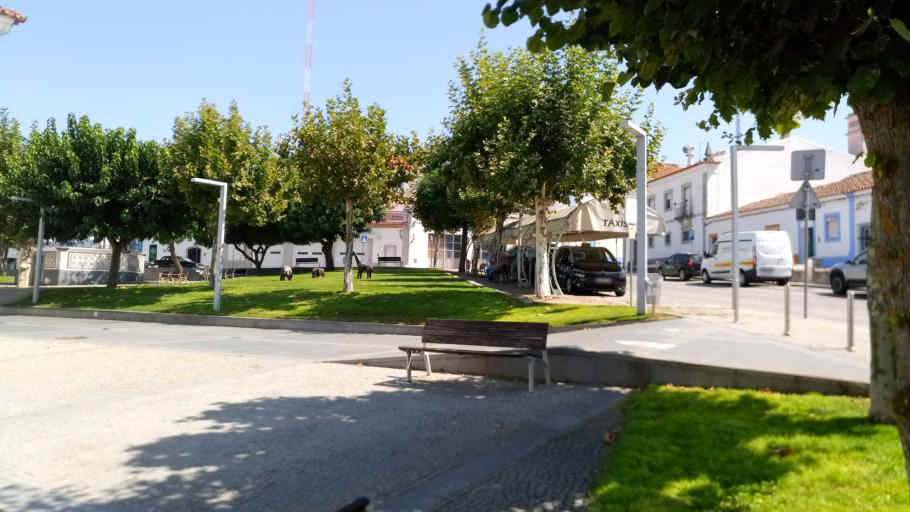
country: PT
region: Evora
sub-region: Arraiolos
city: Arraiolos
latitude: 38.7232
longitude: -7.9843
